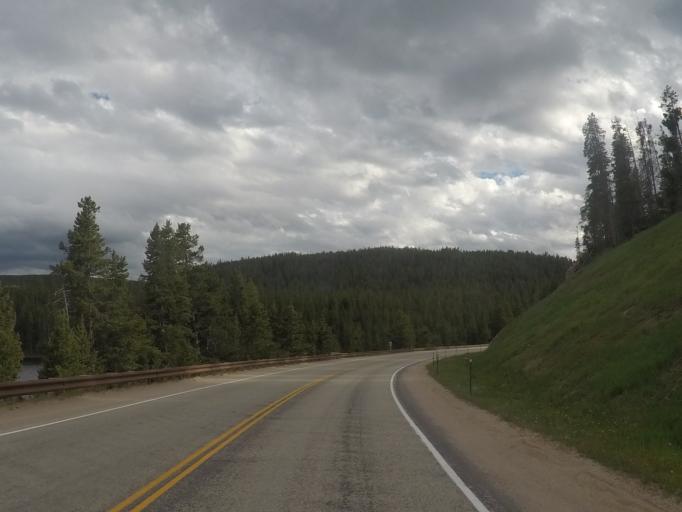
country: US
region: Wyoming
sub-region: Sheridan County
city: Sheridan
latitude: 44.7629
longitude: -107.4381
